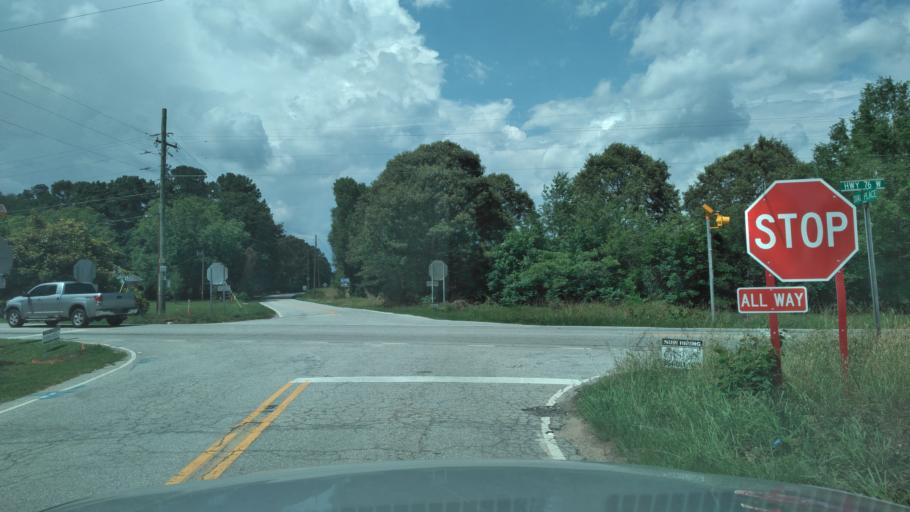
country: US
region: South Carolina
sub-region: Laurens County
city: Laurens
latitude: 34.5143
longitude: -82.0937
